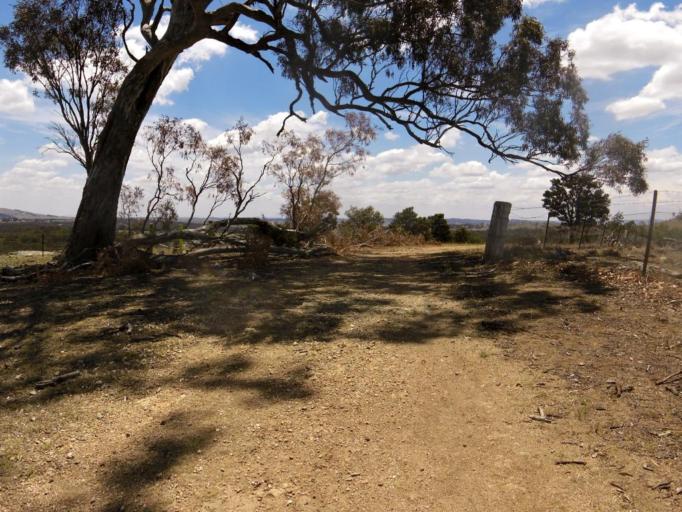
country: AU
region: Australian Capital Territory
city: Kaleen
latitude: -35.1439
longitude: 149.1465
